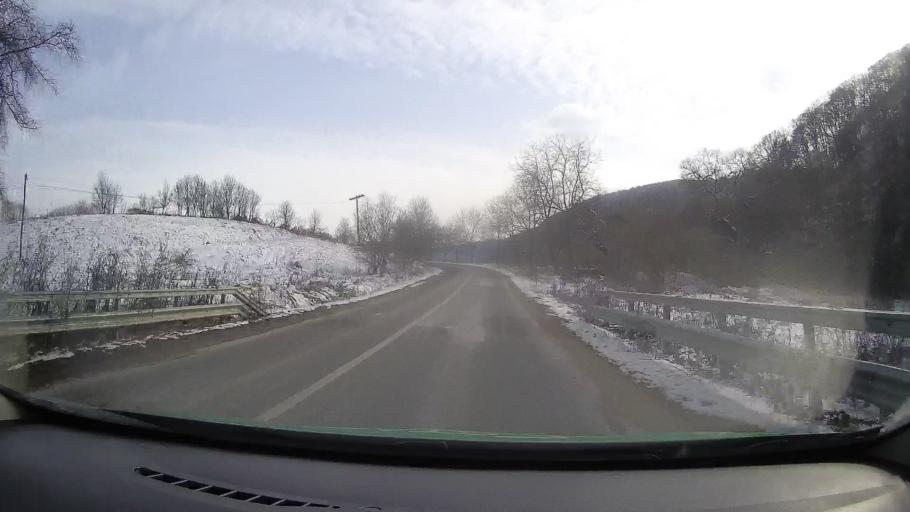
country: RO
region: Mures
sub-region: Comuna Apold
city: Saes
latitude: 46.1641
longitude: 24.7589
